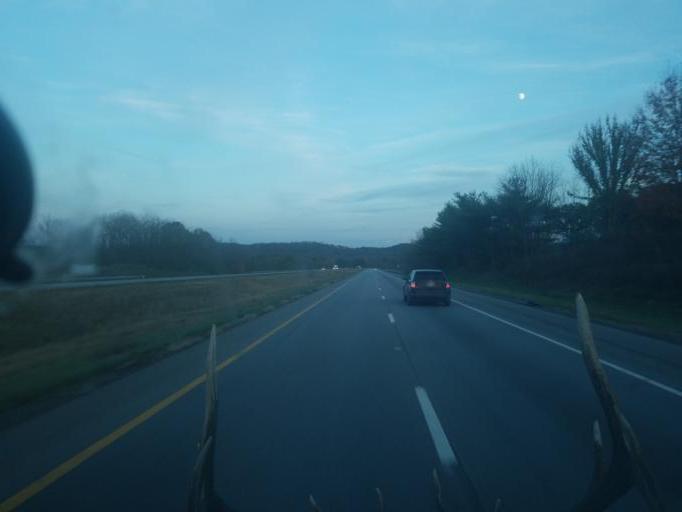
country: US
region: Ohio
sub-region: Muskingum County
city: New Concord
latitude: 39.9848
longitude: -81.6971
